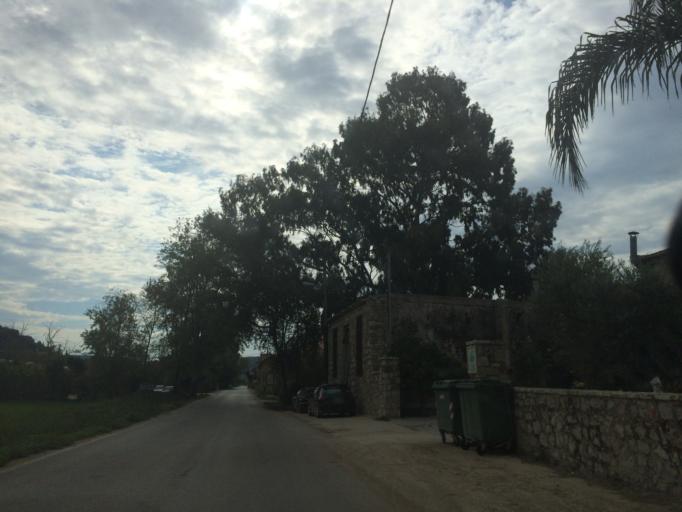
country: GR
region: Peloponnese
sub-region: Nomos Messinias
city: Pylos
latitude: 36.9504
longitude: 21.7025
